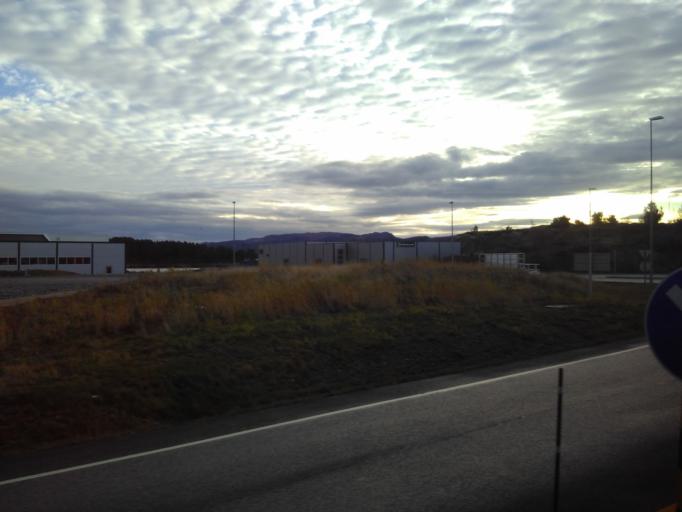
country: NO
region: Sor-Trondelag
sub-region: Hitra
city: Fillan
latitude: 63.5195
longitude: 9.1098
